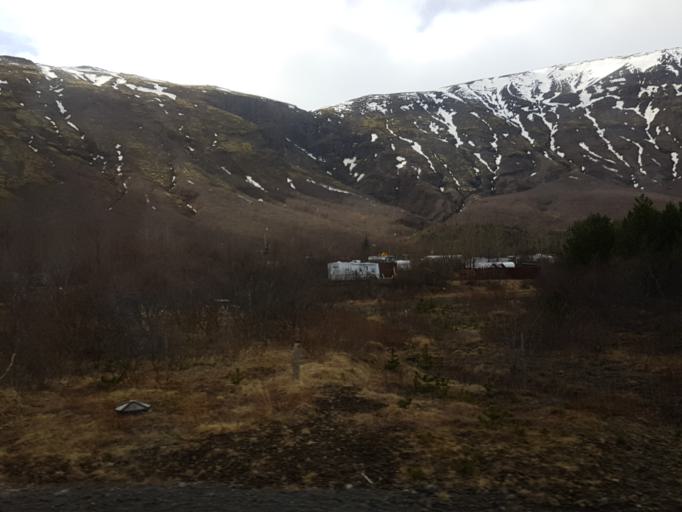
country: IS
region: South
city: Selfoss
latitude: 64.2266
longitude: -20.7219
